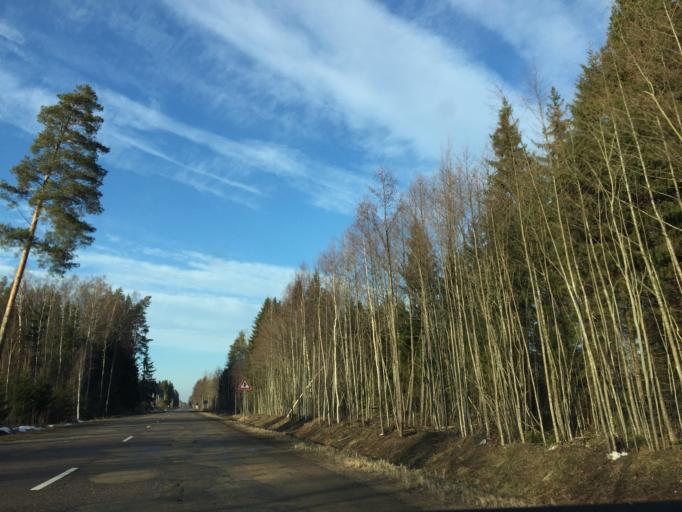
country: LV
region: Lecava
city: Iecava
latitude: 56.7027
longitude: 24.1139
